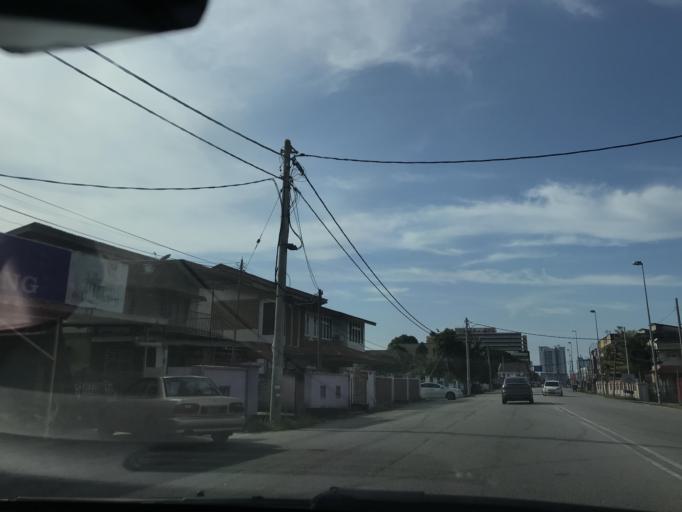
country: MY
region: Kelantan
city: Kota Bharu
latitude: 6.1178
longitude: 102.2471
